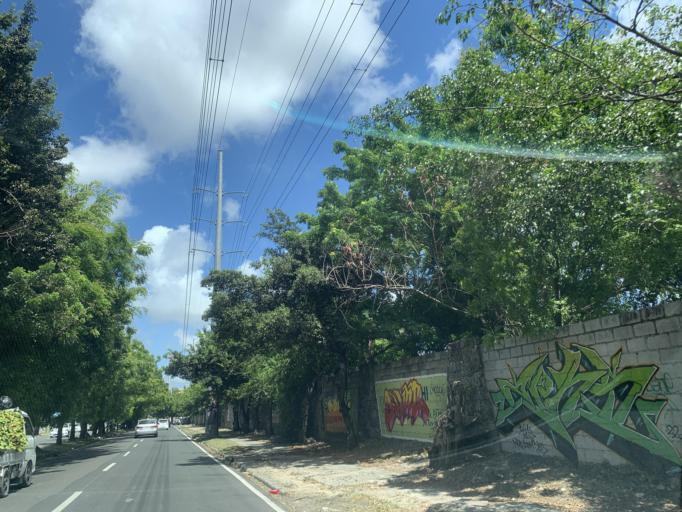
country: DO
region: Nacional
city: La Agustina
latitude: 18.5056
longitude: -69.9235
